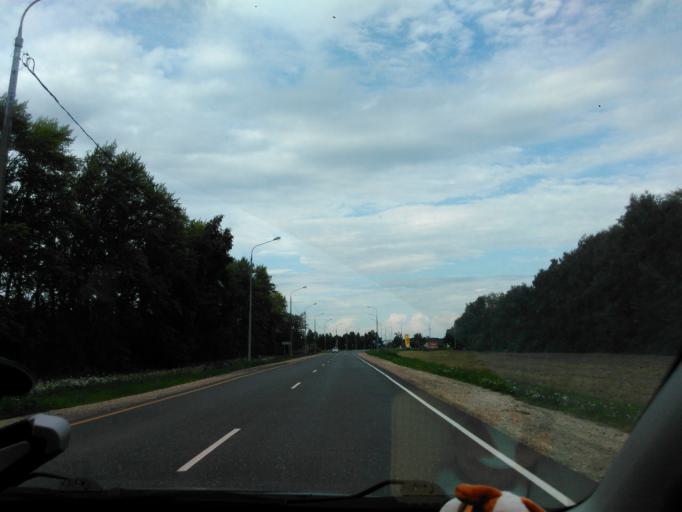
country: RU
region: Penza
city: Lermontovo
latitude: 52.9695
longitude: 43.5856
